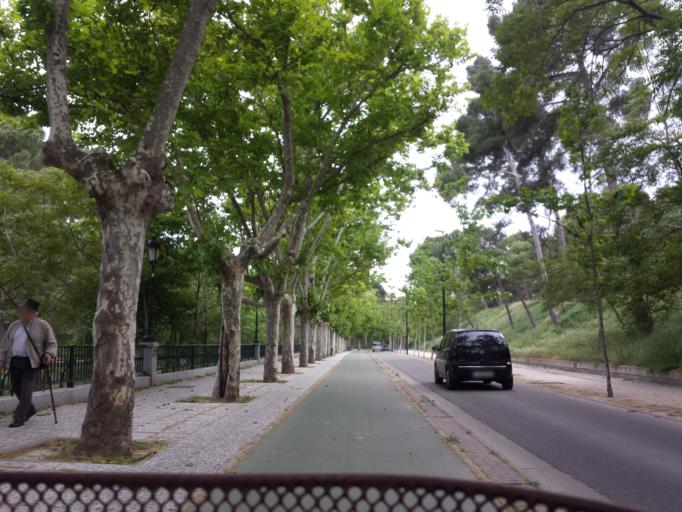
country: ES
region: Aragon
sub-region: Provincia de Zaragoza
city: Delicias
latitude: 41.6314
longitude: -0.8918
